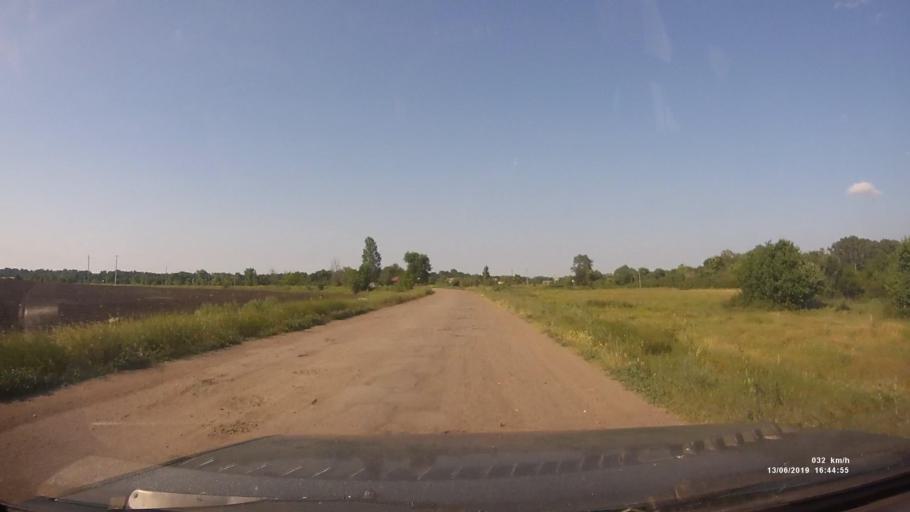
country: RU
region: Rostov
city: Kazanskaya
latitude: 49.9467
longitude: 41.4217
